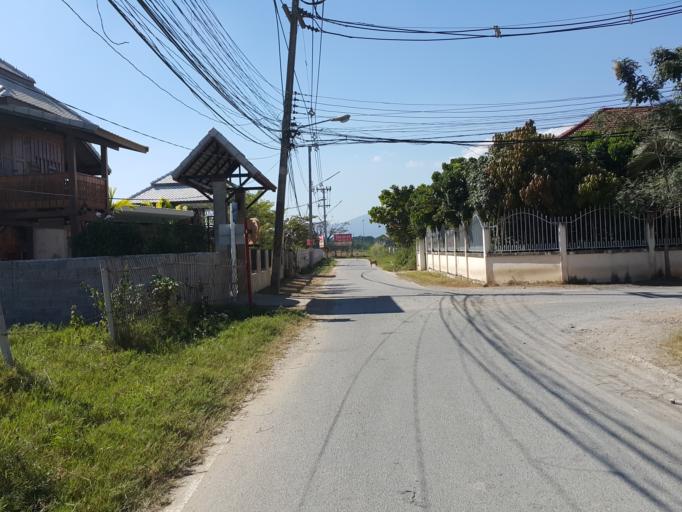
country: TH
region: Chiang Mai
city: Chiang Mai
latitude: 18.7753
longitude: 99.0355
